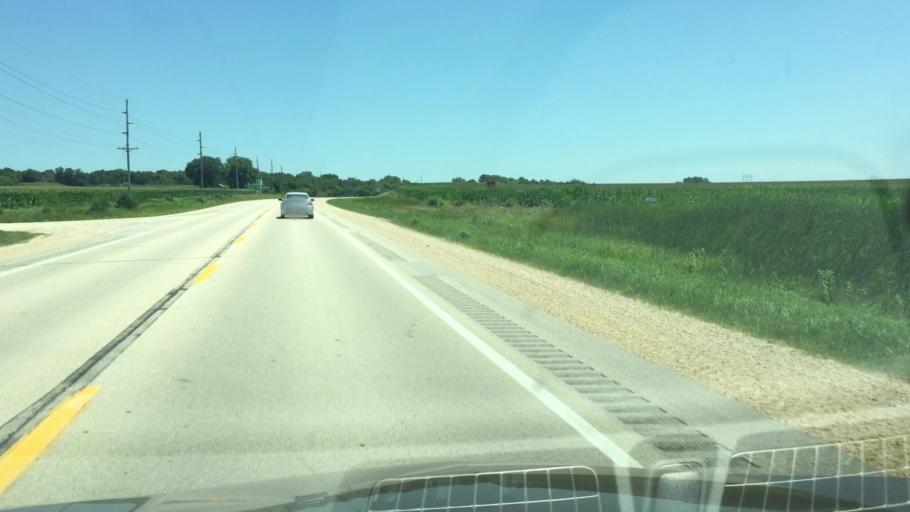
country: US
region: Iowa
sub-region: Jackson County
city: Maquoketa
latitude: 42.0650
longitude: -90.7680
